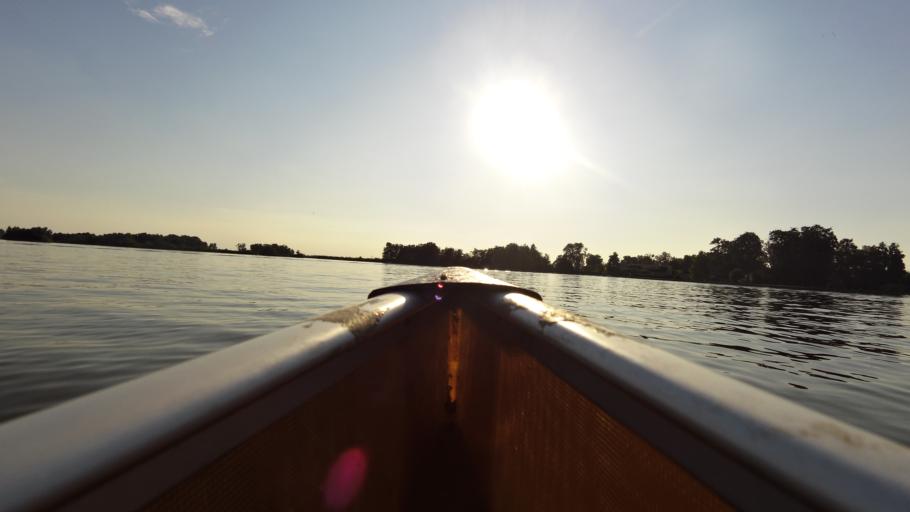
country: NL
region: South Holland
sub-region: Gemeente Nieuwkoop
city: Nieuwkoop
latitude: 52.1294
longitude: 4.7663
